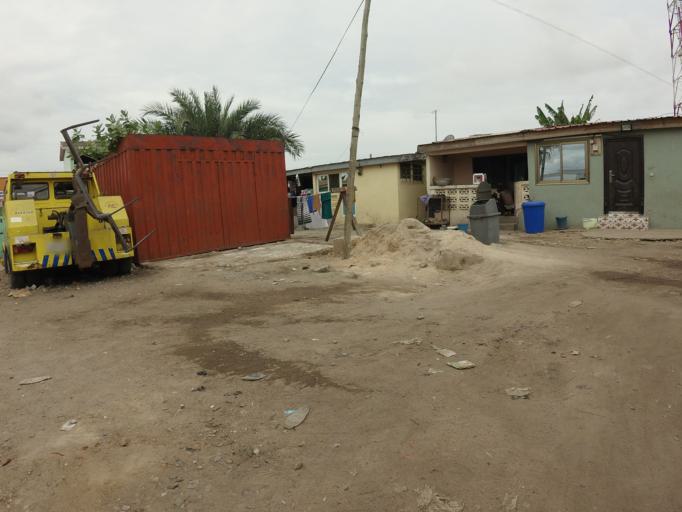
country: GH
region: Greater Accra
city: Accra
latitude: 5.5919
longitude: -0.2146
